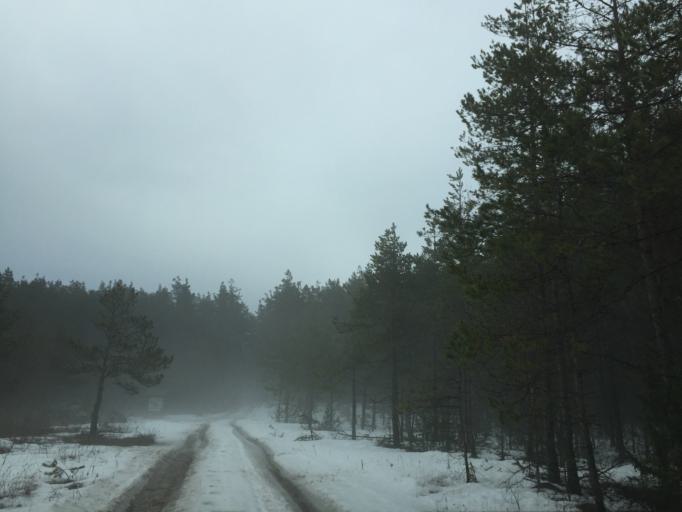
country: EE
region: Saare
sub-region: Orissaare vald
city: Orissaare
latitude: 58.6140
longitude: 22.9502
